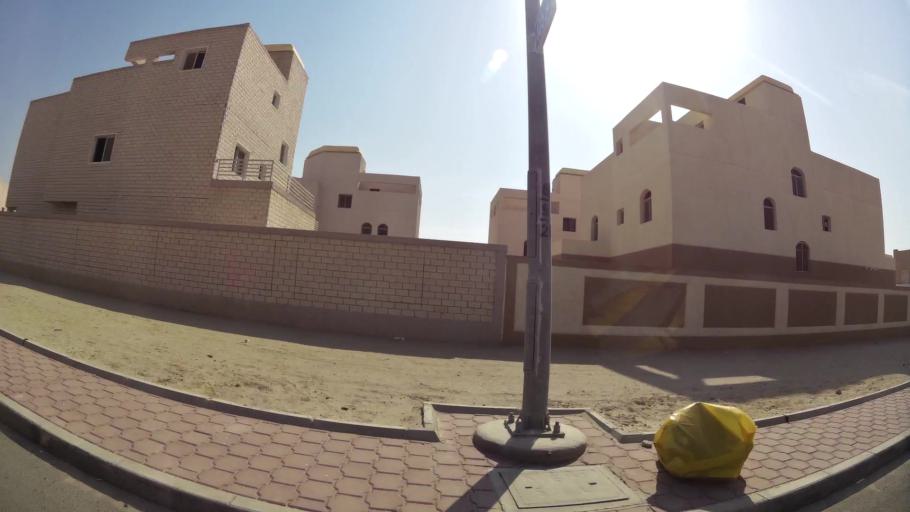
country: KW
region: Al Ahmadi
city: Al Wafrah
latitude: 28.7991
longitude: 48.0784
